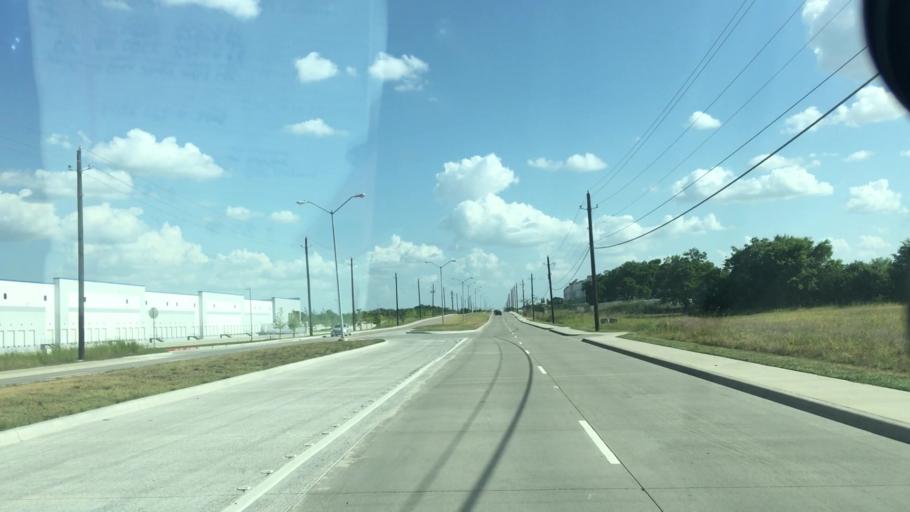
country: US
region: Texas
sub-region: Dallas County
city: Lancaster
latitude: 32.6326
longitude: -96.7524
